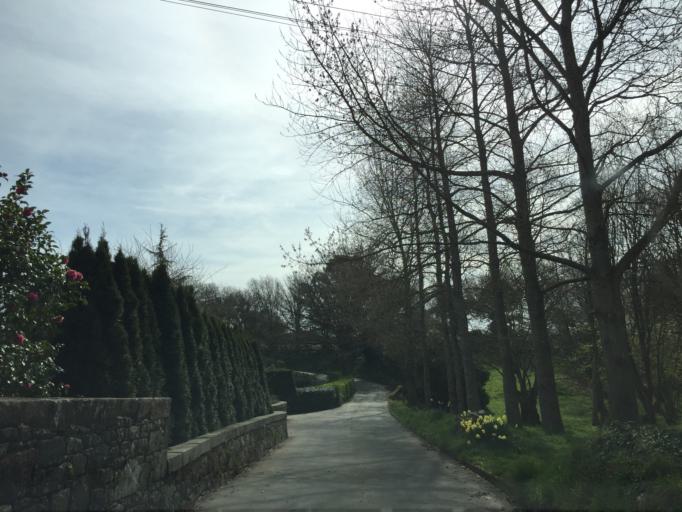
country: JE
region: St Helier
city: Saint Helier
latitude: 49.2278
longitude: -2.1217
